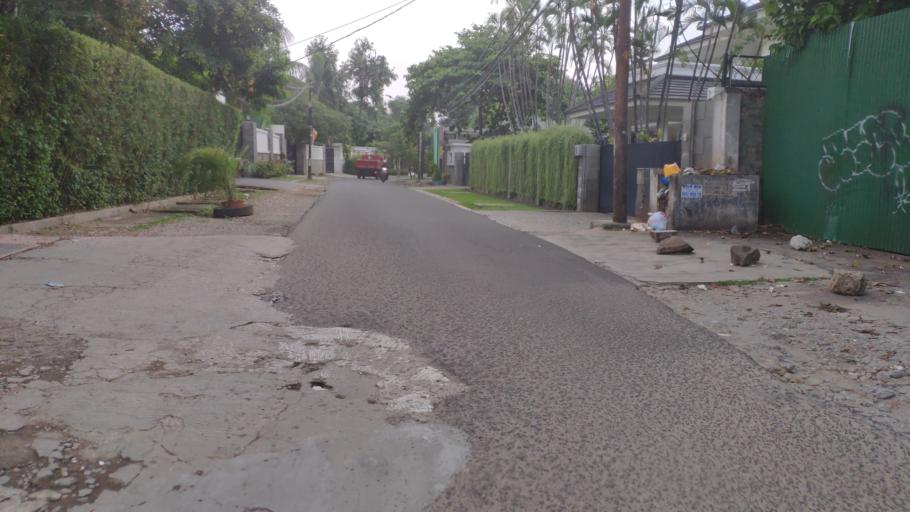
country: ID
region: Jakarta Raya
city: Jakarta
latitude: -6.2752
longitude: 106.8245
